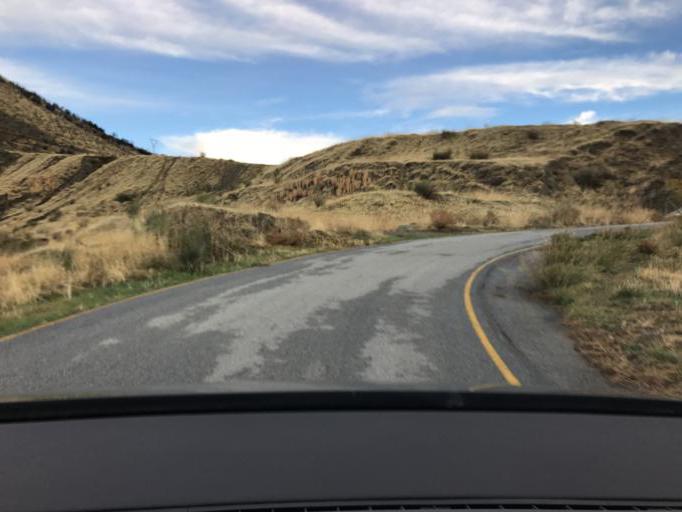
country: ES
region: Andalusia
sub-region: Provincia de Granada
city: Cenes de la Vega
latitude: 37.1665
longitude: -3.5380
